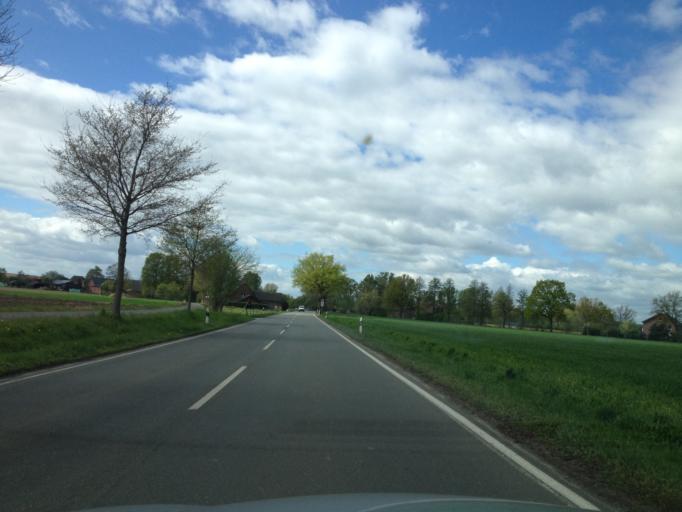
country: DE
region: North Rhine-Westphalia
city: Rietberg
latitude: 51.8143
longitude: 8.4621
